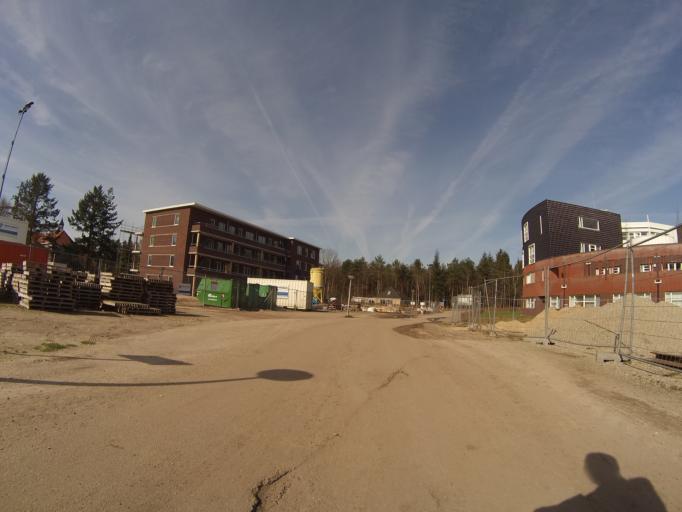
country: NL
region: Utrecht
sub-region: Gemeente Zeist
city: Zeist
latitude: 52.1153
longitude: 5.2754
